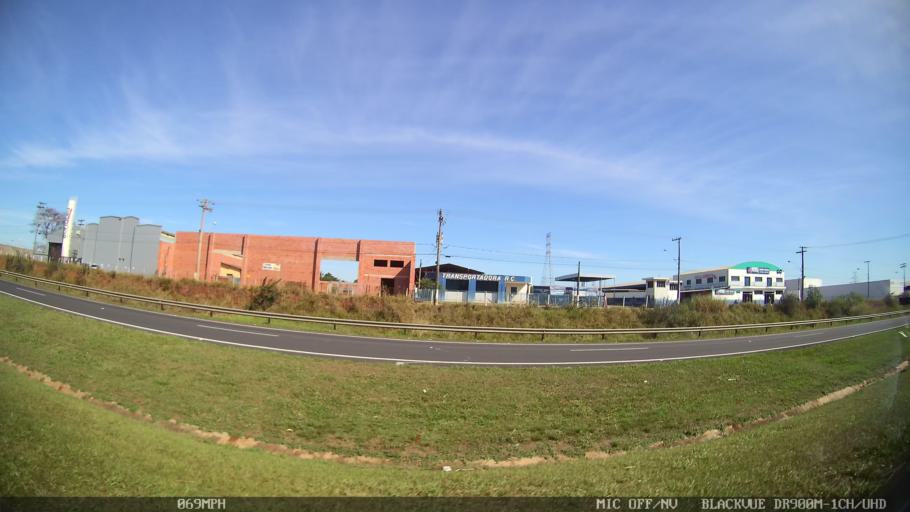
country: BR
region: Sao Paulo
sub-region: Porto Ferreira
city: Porto Ferreira
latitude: -21.8731
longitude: -47.4883
